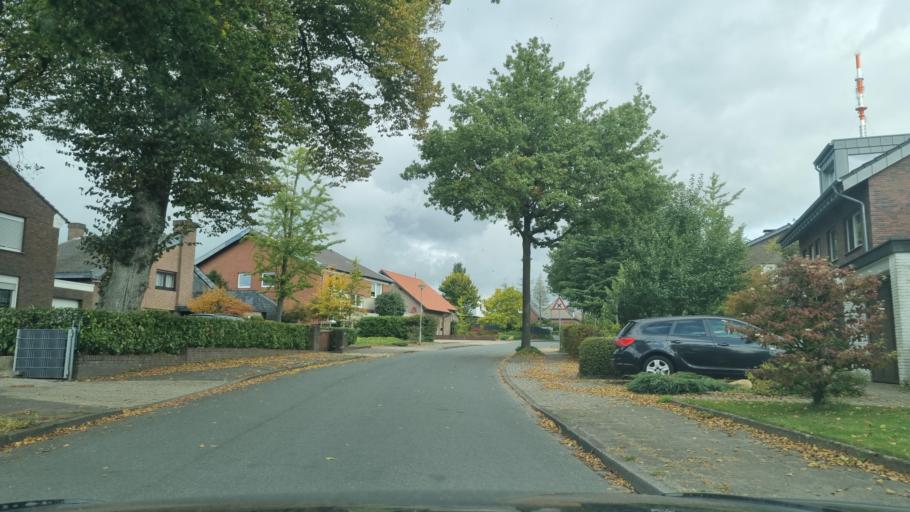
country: DE
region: North Rhine-Westphalia
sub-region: Regierungsbezirk Dusseldorf
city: Kleve
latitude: 51.7851
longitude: 6.1066
